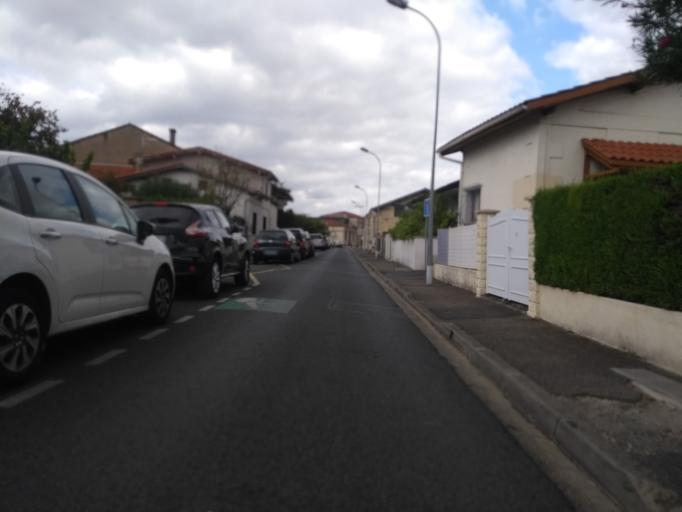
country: FR
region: Aquitaine
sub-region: Departement de la Gironde
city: Begles
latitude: 44.8066
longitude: -0.5665
